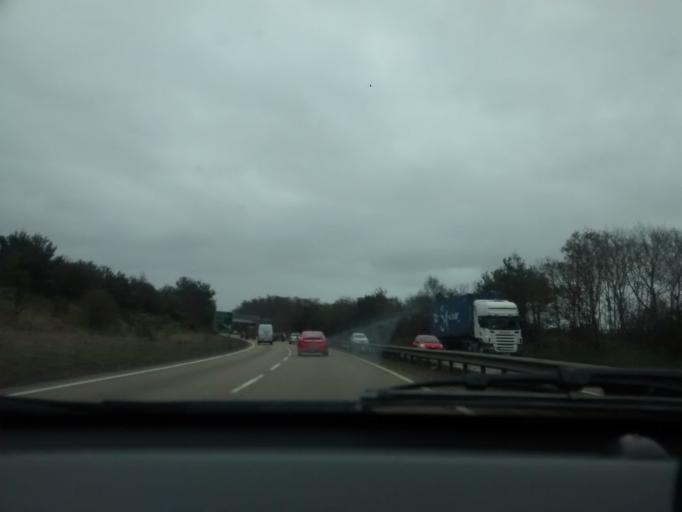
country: GB
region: England
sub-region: Suffolk
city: Kesgrave
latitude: 52.0243
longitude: 1.2323
